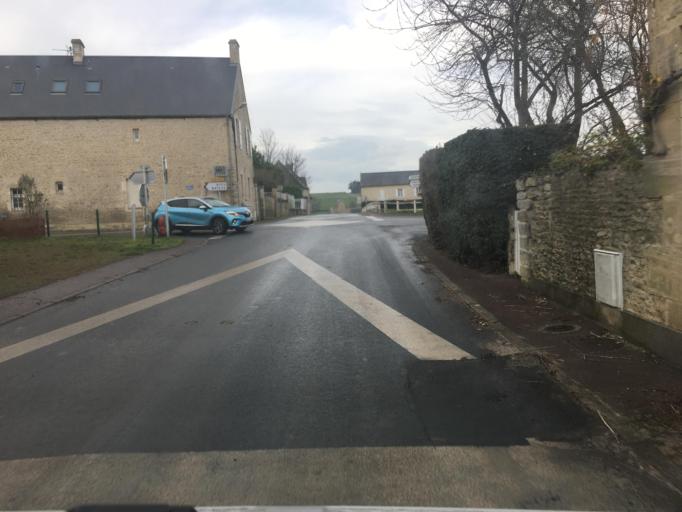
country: FR
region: Lower Normandy
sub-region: Departement du Calvados
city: Ver-sur-Mer
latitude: 49.3307
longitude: -0.6033
